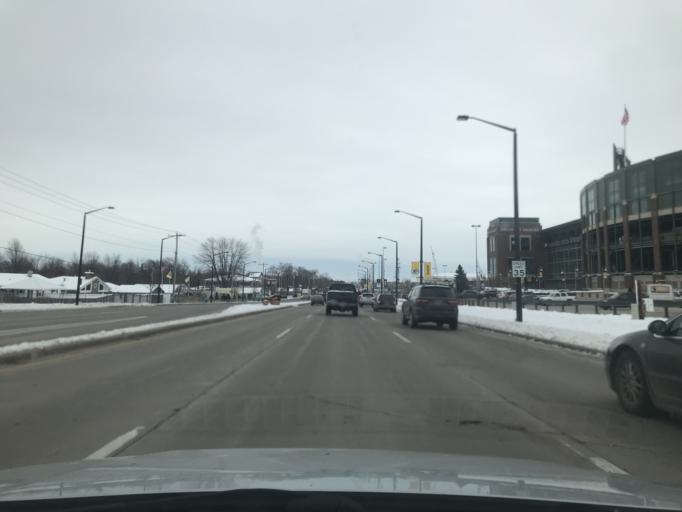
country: US
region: Wisconsin
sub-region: Brown County
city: Ashwaubenon
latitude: 44.5036
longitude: -88.0630
